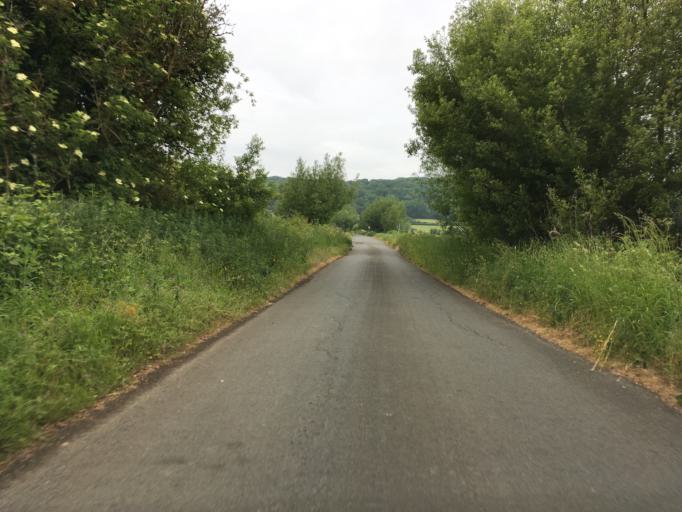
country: GB
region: England
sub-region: North Somerset
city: Clevedon
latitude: 51.4514
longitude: -2.8195
